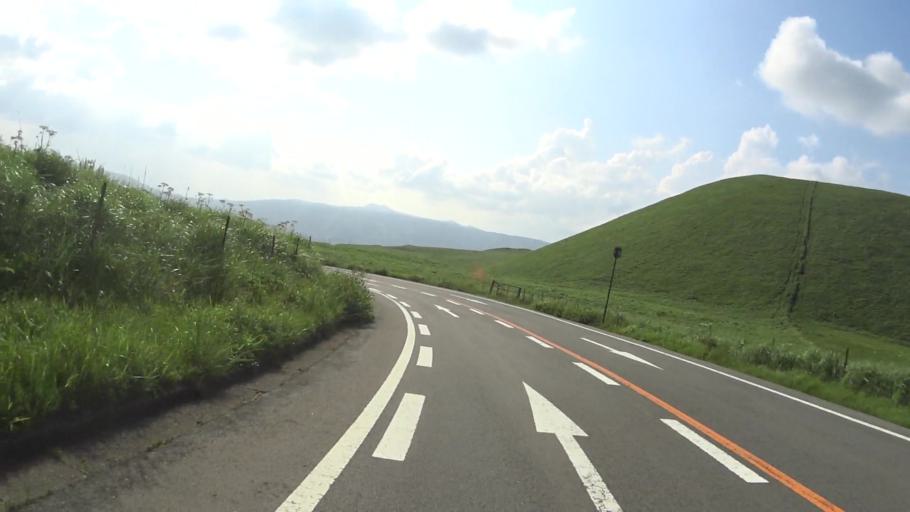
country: JP
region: Kumamoto
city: Aso
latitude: 32.9023
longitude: 131.0450
